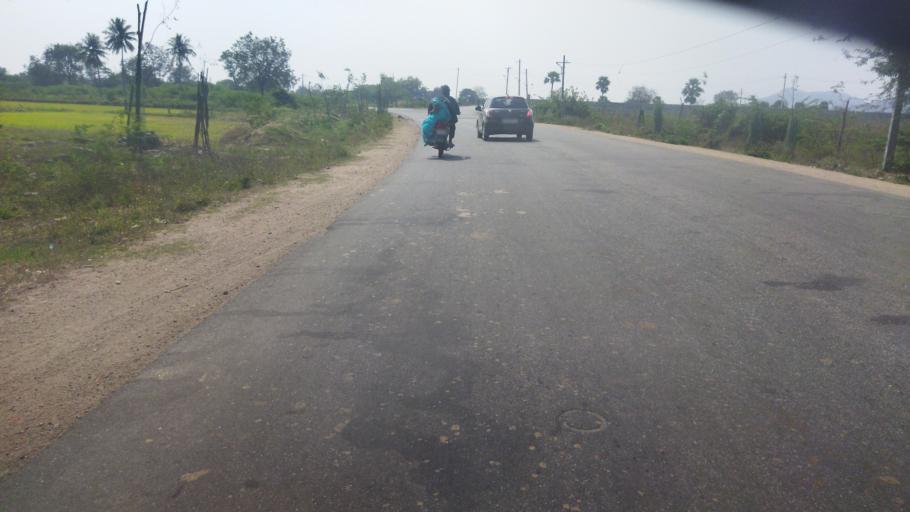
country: IN
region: Telangana
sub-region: Nalgonda
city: Nalgonda
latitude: 17.0848
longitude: 79.2844
